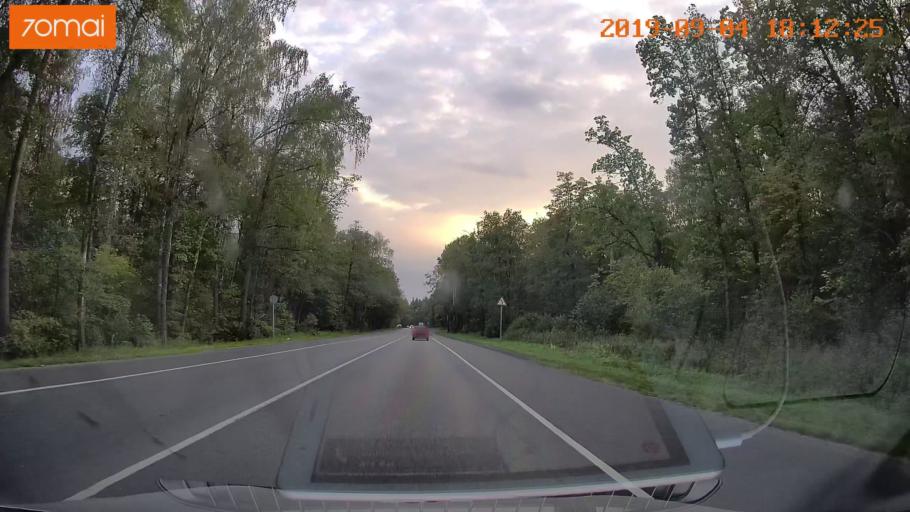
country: RU
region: Moskovskaya
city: Lopatinskiy
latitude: 55.3705
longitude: 38.7421
